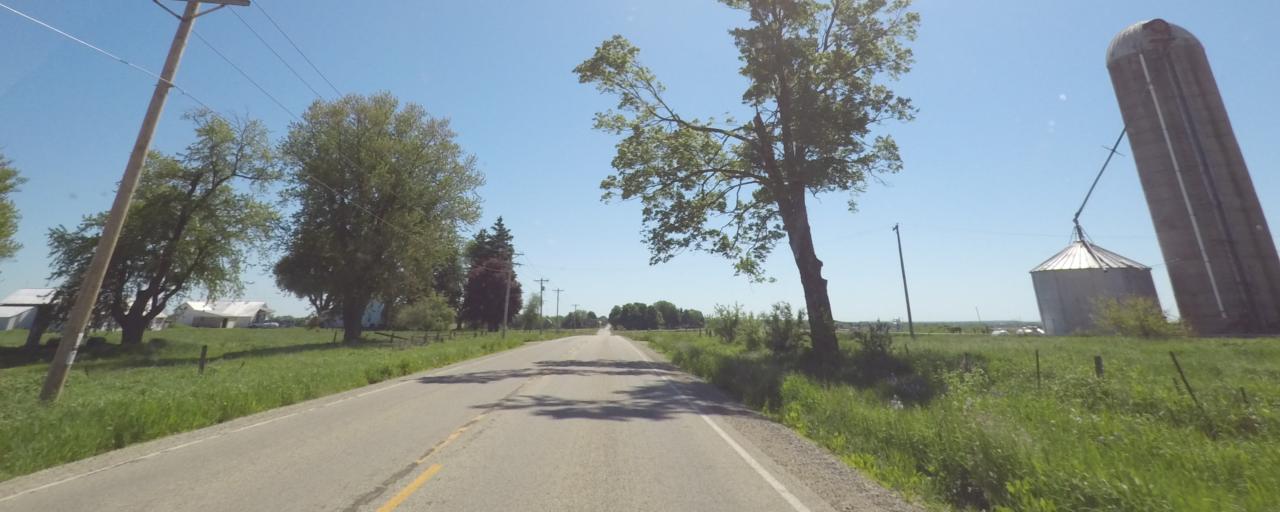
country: US
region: Wisconsin
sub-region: Rock County
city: Evansville
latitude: 42.7875
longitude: -89.3443
